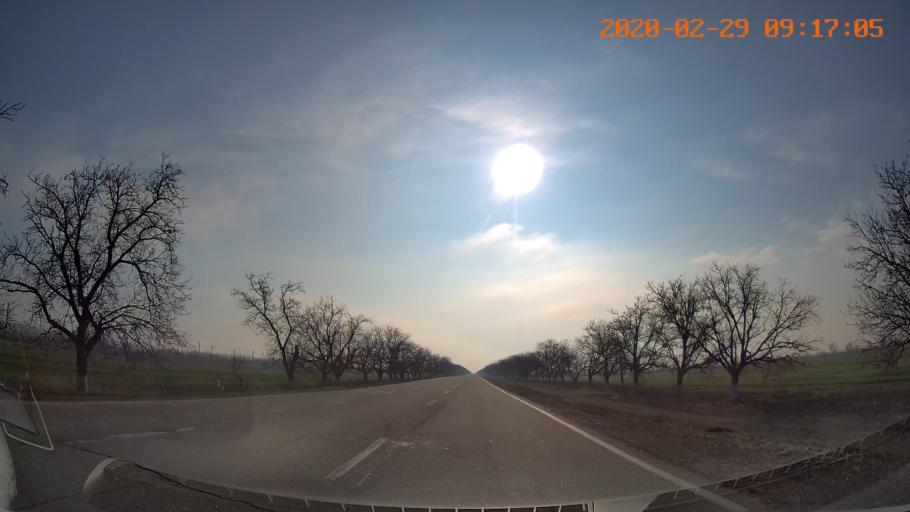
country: MD
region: Telenesti
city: Pervomaisc
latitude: 46.7861
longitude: 29.8979
